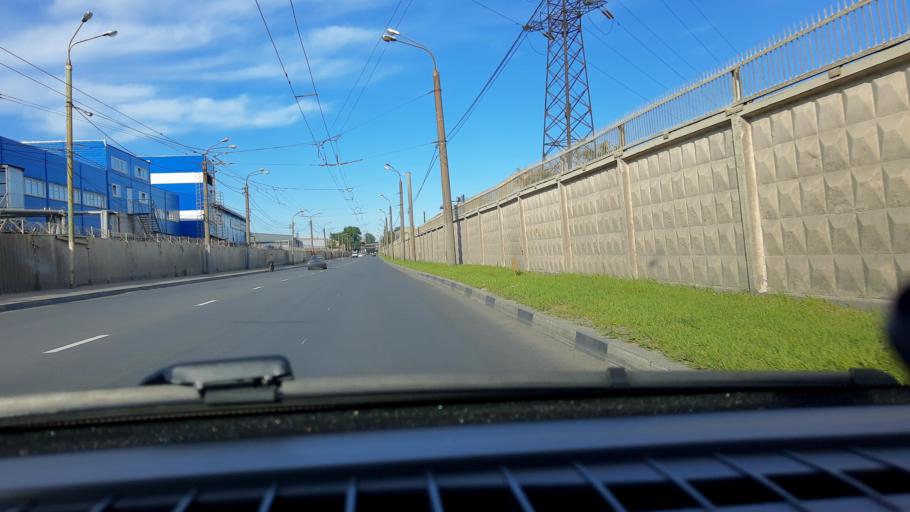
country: RU
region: Nizjnij Novgorod
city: Nizhniy Novgorod
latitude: 56.2409
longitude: 43.8937
